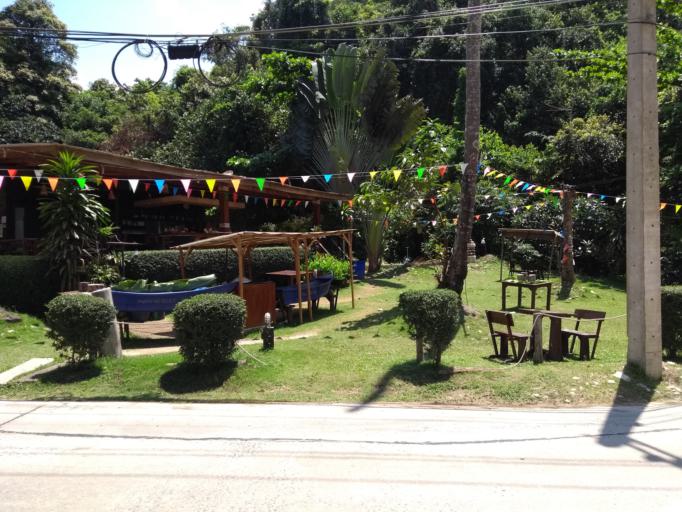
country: TH
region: Trat
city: Ko Kut
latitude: 11.6386
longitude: 102.5441
